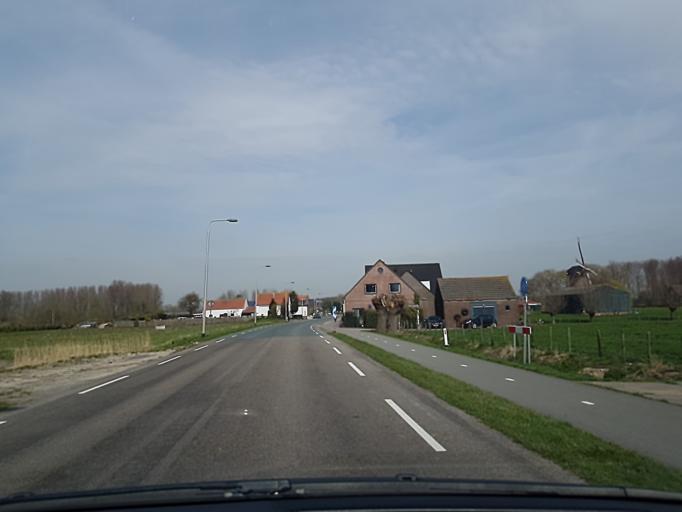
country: NL
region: Zeeland
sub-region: Gemeente Hulst
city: Hulst
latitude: 51.3367
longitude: 4.0341
